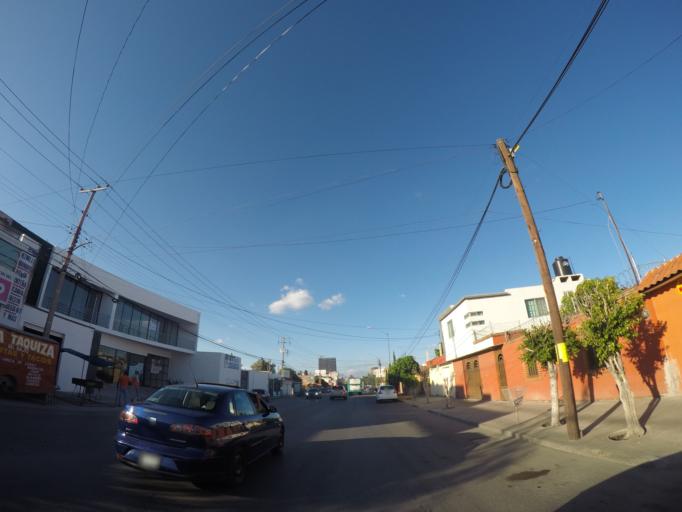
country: MX
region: San Luis Potosi
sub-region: San Luis Potosi
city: San Luis Potosi
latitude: 22.1760
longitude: -100.9976
